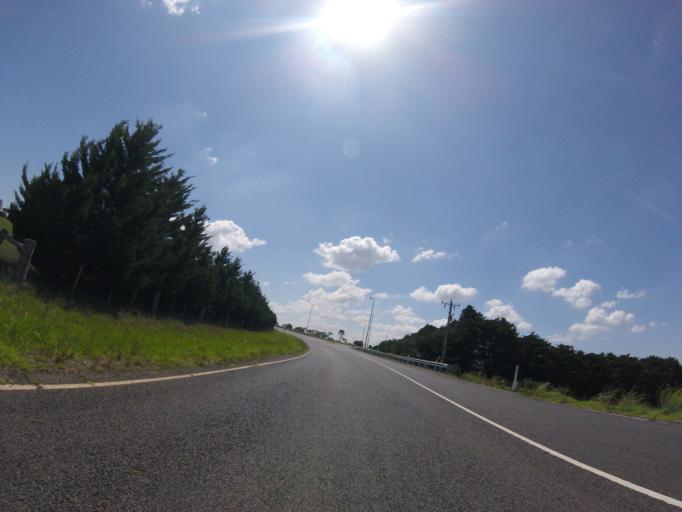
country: AU
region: Victoria
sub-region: Hume
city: Greenvale
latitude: -37.6211
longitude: 144.8195
